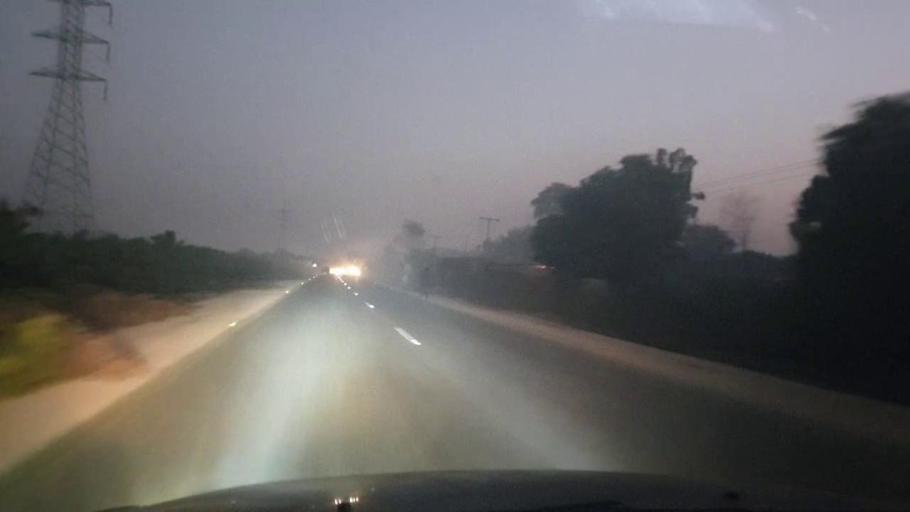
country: PK
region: Sindh
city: Chambar
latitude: 25.3666
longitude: 68.7835
